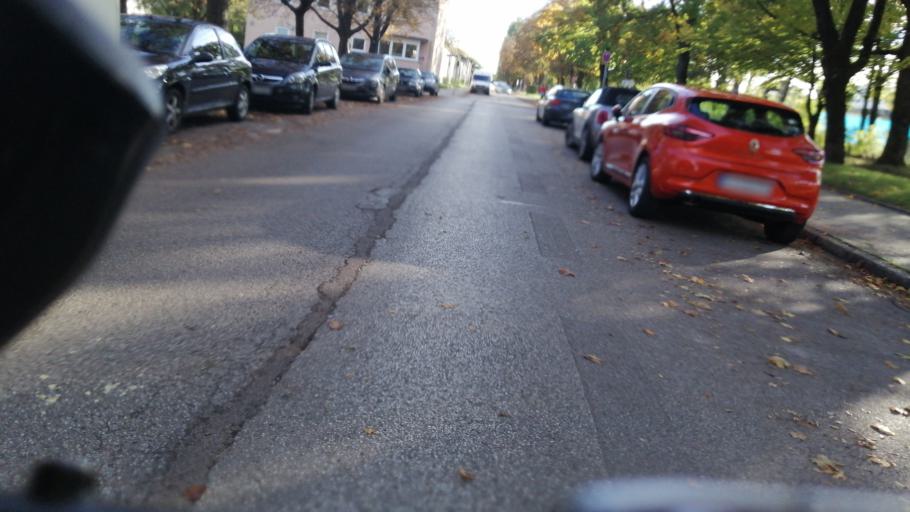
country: DE
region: Bavaria
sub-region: Upper Bavaria
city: Unterfoehring
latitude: 48.1930
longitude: 11.6126
